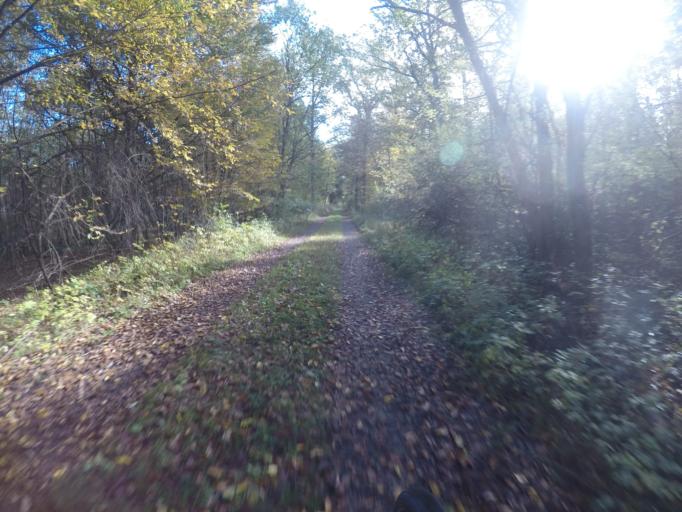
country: DE
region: Baden-Wuerttemberg
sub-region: Regierungsbezirk Stuttgart
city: Ehningen
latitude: 48.6737
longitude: 8.9598
